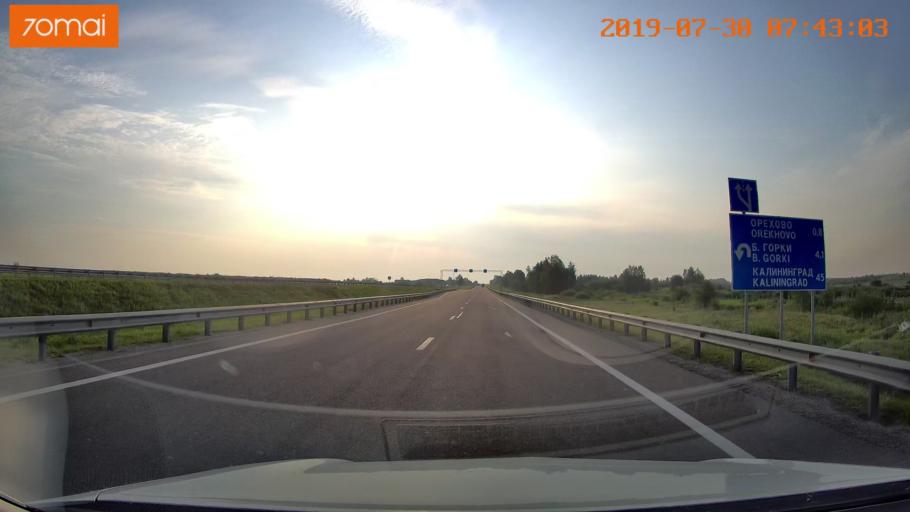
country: RU
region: Kaliningrad
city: Gvardeysk
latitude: 54.6487
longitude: 21.2956
